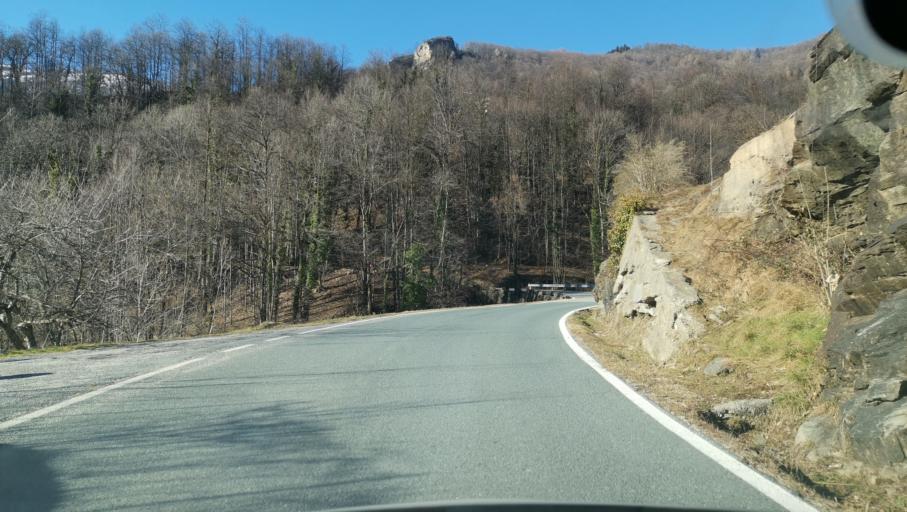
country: IT
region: Piedmont
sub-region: Provincia di Torino
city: Rora
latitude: 44.7887
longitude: 7.2003
